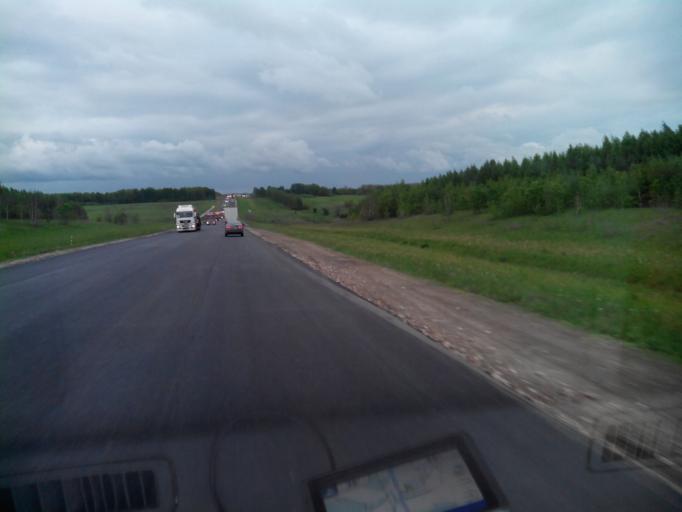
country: RU
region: Penza
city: Gorodishche
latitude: 53.2501
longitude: 45.4952
